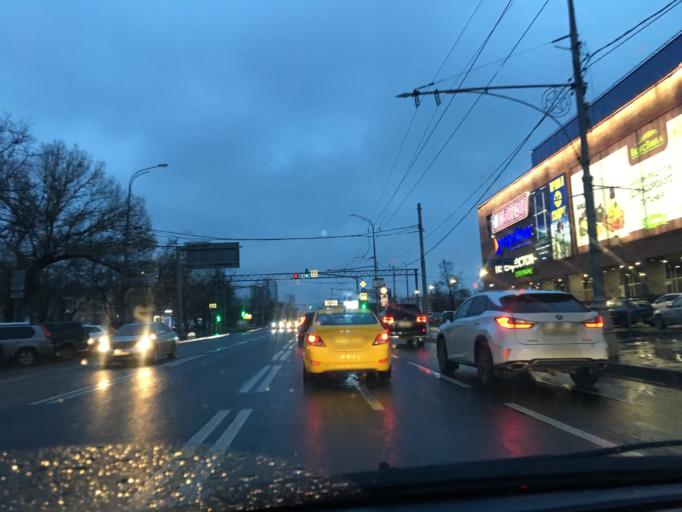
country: RU
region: Moscow
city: Mar'ina Roshcha
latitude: 55.7955
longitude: 37.6162
